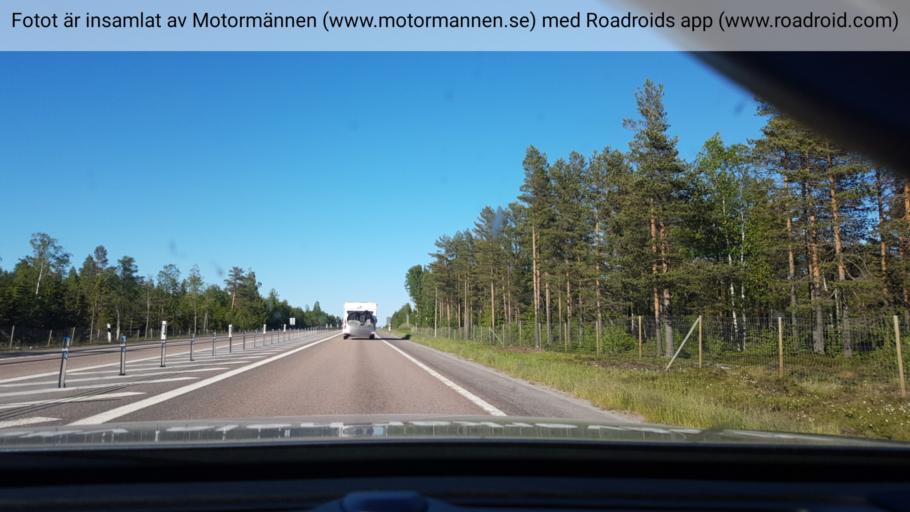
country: SE
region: Vaesternorrland
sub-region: Haernoesands Kommun
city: Haernoesand
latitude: 62.5671
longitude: 17.7356
